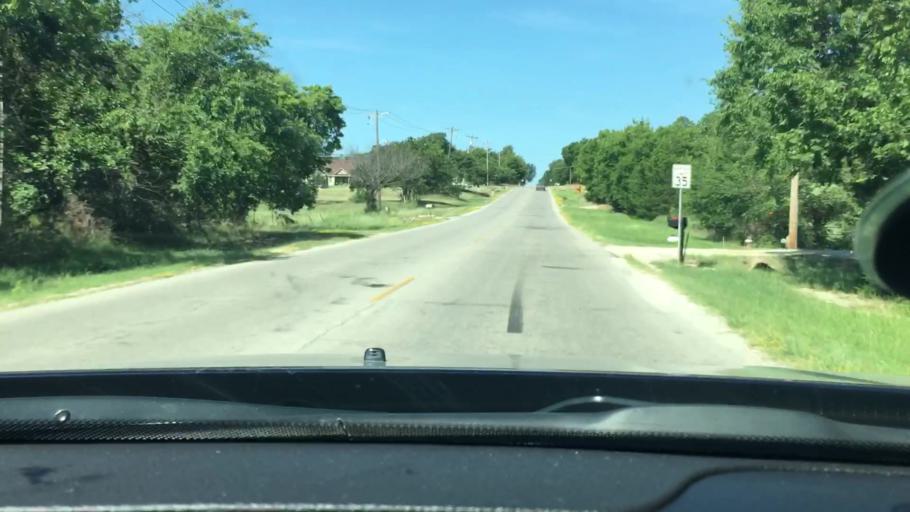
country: US
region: Oklahoma
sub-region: Carter County
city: Ardmore
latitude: 34.1584
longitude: -97.1098
